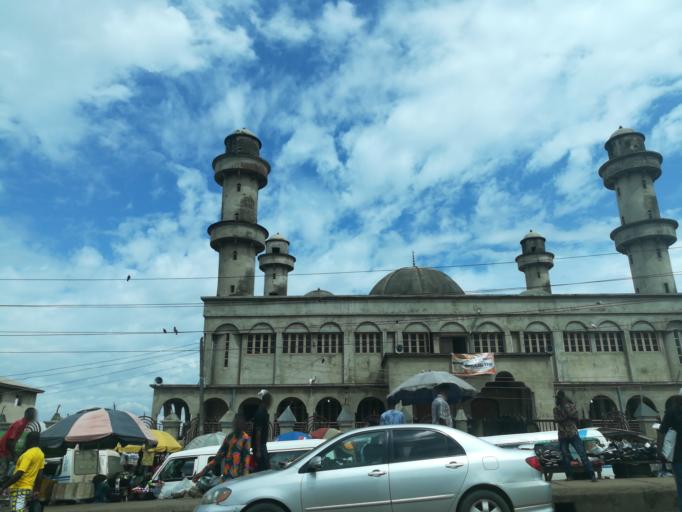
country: NG
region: Lagos
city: Ikorodu
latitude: 6.6210
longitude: 3.5038
